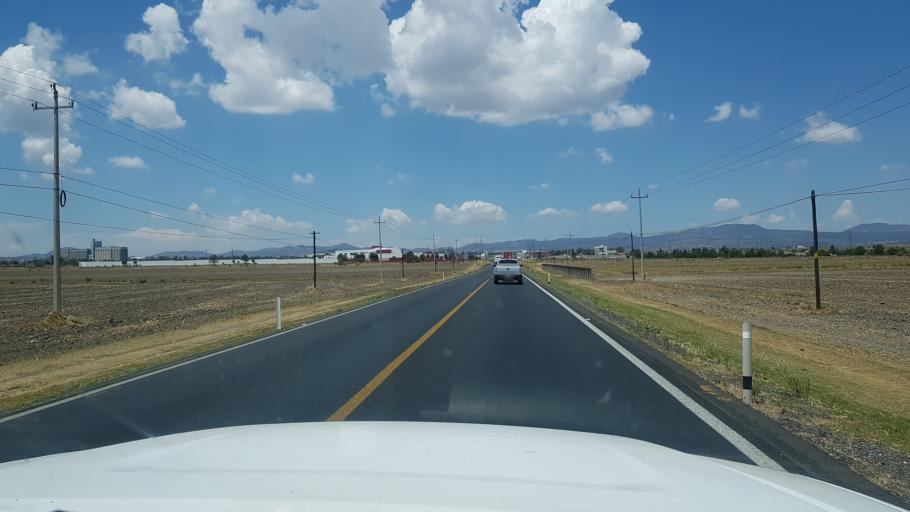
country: MX
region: Hidalgo
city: Calpulalpan
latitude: 19.5815
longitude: -98.5315
